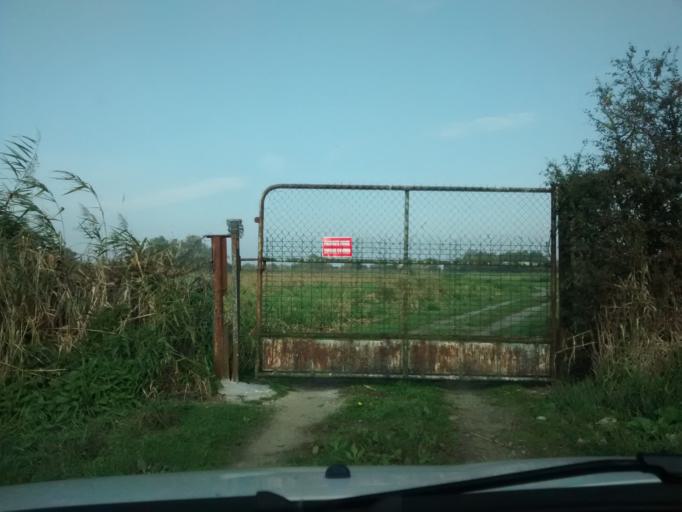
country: FR
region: Pays de la Loire
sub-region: Departement de la Loire-Atlantique
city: Cordemais
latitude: 47.2479
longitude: -1.8749
